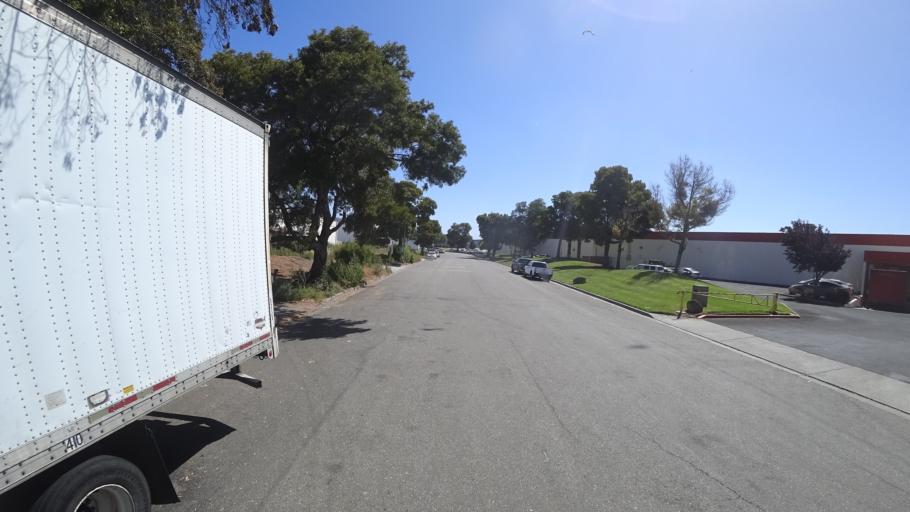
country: US
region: California
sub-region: Alameda County
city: San Lorenzo
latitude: 37.6588
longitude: -122.1335
